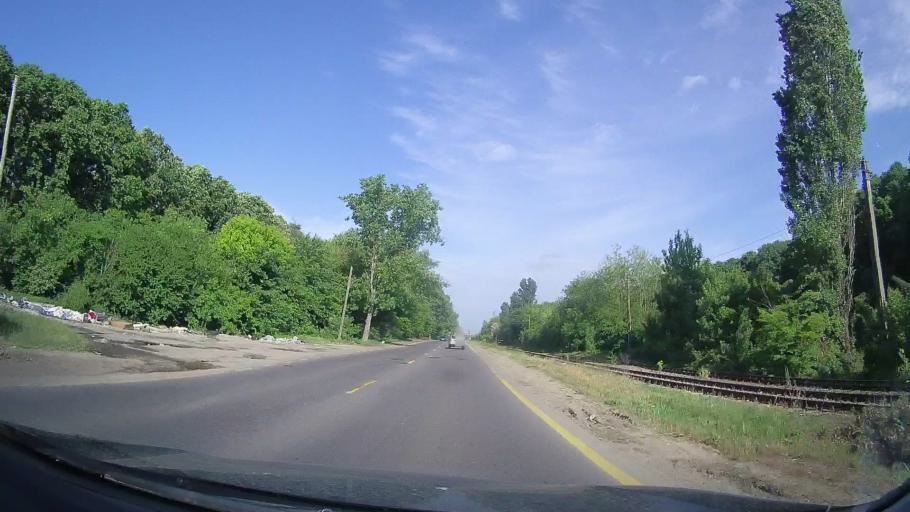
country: RO
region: Ilfov
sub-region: Comuna Magurele
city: Magurele
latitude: 44.3556
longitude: 26.0477
